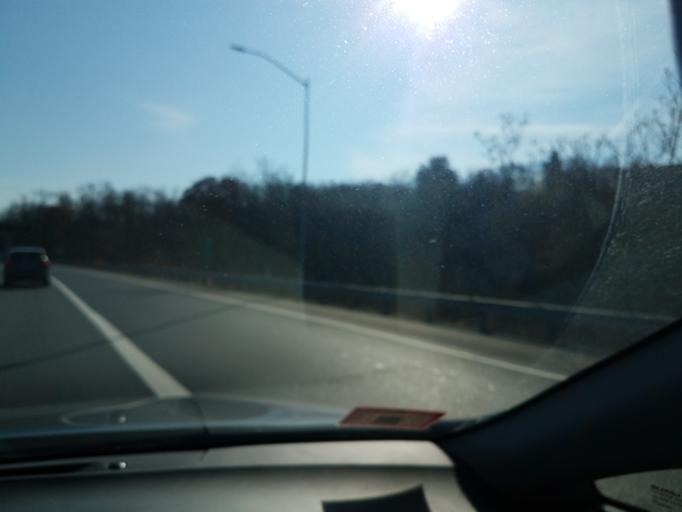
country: US
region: Pennsylvania
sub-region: Allegheny County
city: Bellevue
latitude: 40.5104
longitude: -80.0490
